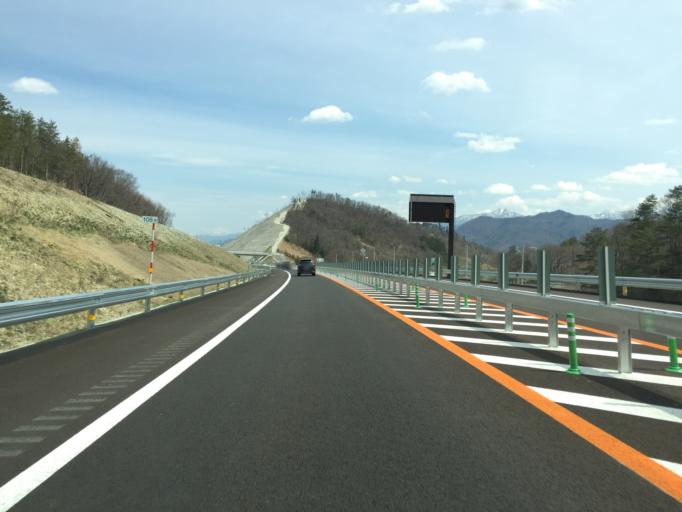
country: JP
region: Yamagata
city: Kaminoyama
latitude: 38.1150
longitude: 140.2457
